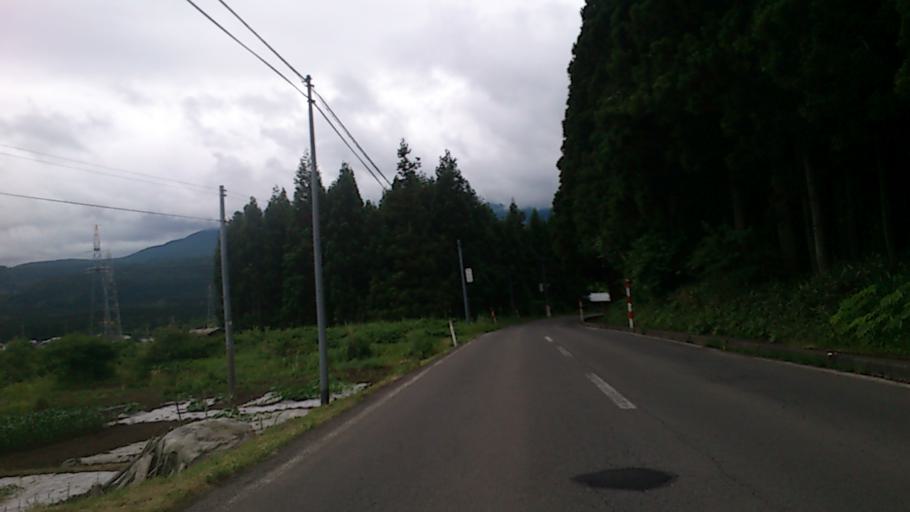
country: JP
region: Yamagata
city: Yuza
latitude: 39.1798
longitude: 139.9466
